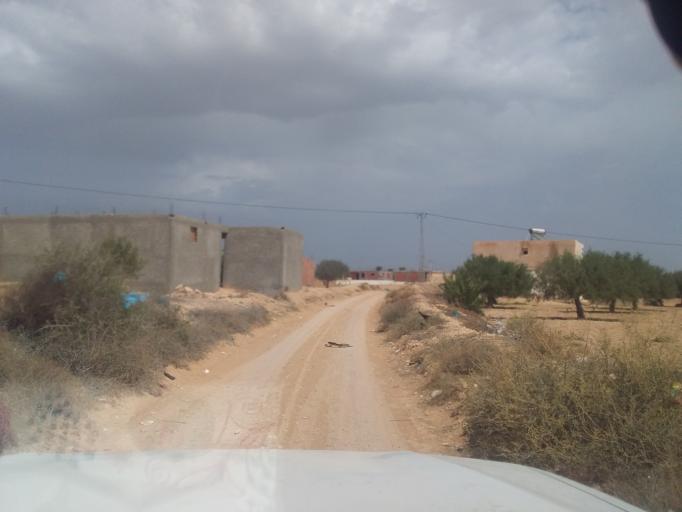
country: TN
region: Madanin
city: Medenine
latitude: 33.5908
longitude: 10.3253
